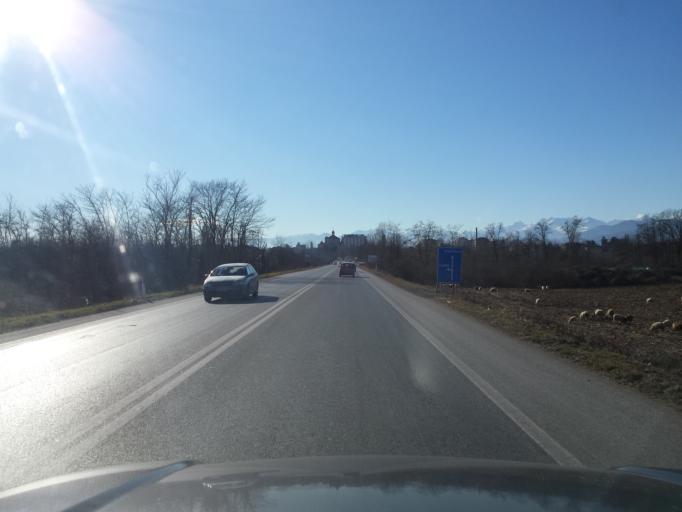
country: IT
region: Piedmont
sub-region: Provincia di Torino
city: Ozegna
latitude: 45.3376
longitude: 7.7370
